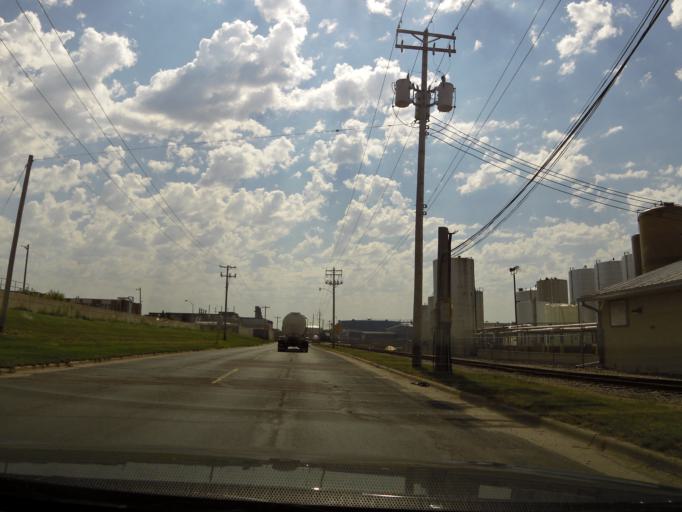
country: US
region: Minnesota
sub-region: Dakota County
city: South Saint Paul
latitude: 44.9306
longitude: -93.0463
